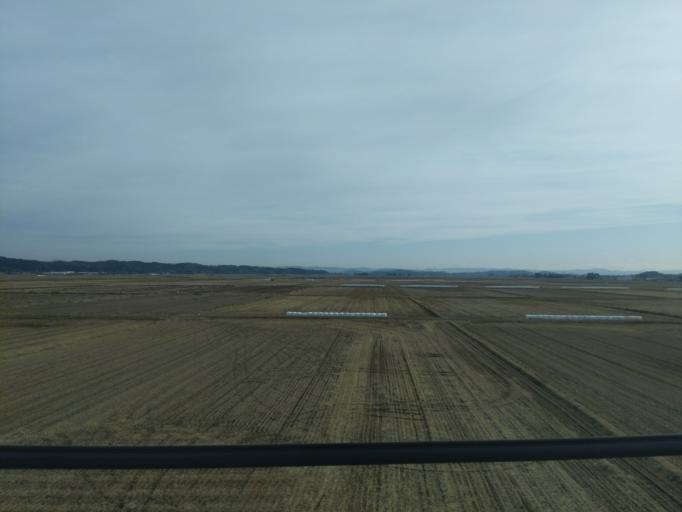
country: JP
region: Iwate
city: Ichinoseki
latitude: 38.7946
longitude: 141.0947
